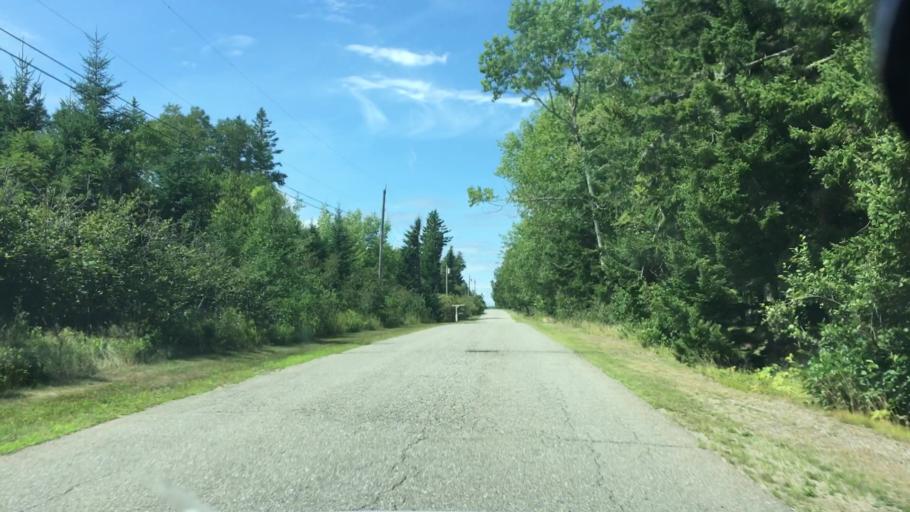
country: US
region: Maine
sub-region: Washington County
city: Eastport
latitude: 44.9317
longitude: -67.0424
